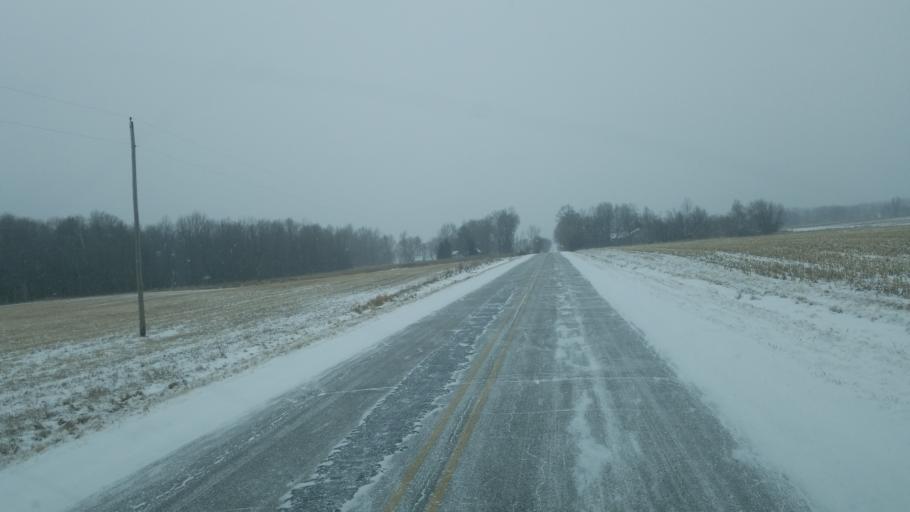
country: US
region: Michigan
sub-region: Mecosta County
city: Big Rapids
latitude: 43.7662
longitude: -85.4029
